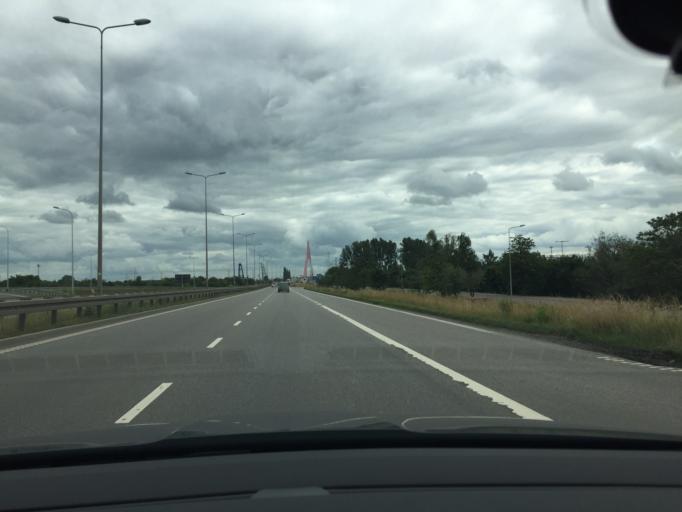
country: PL
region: Pomeranian Voivodeship
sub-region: Gdansk
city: Gdansk
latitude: 54.3673
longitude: 18.6872
